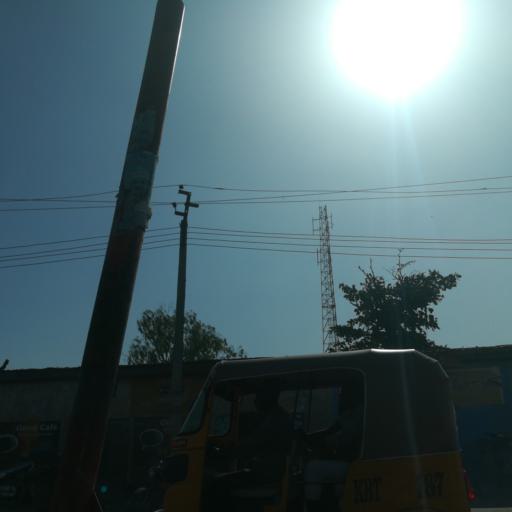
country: NG
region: Kano
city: Kano
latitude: 12.0119
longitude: 8.5212
